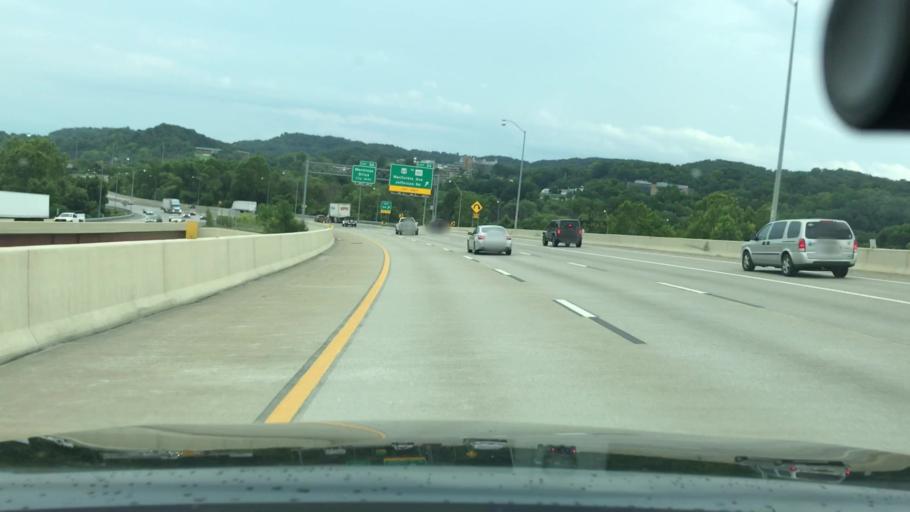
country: US
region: West Virginia
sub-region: Kanawha County
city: South Charleston
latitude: 38.3602
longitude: -81.7171
